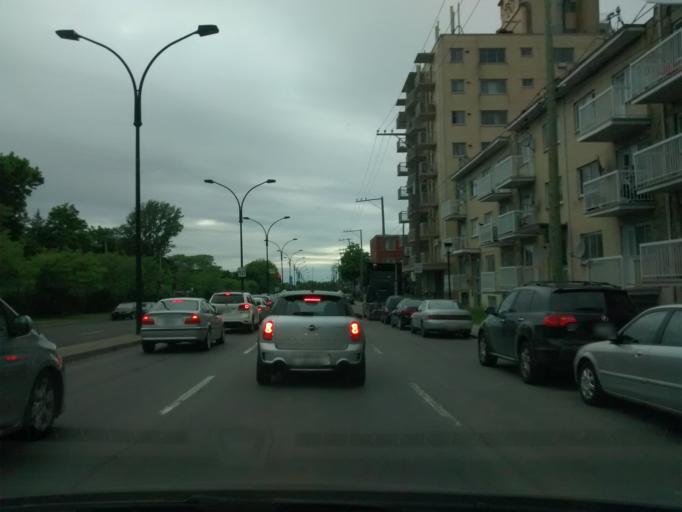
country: CA
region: Quebec
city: Mont-Royal
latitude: 45.5292
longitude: -73.6429
